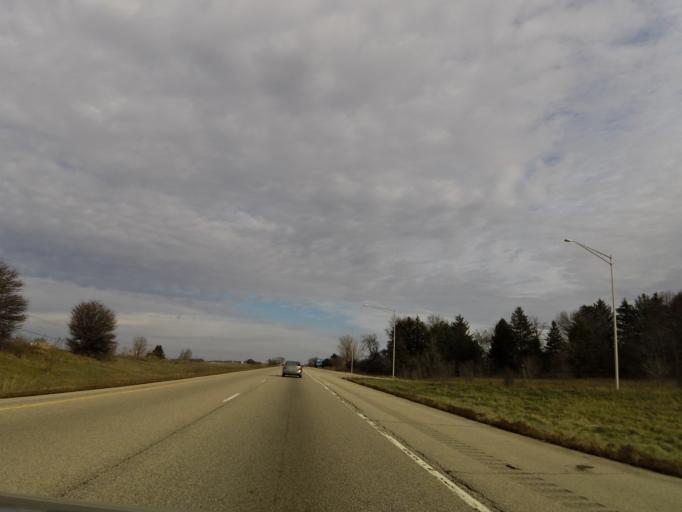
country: US
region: Wisconsin
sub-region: Rock County
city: Beloit
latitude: 42.5073
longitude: -88.9843
